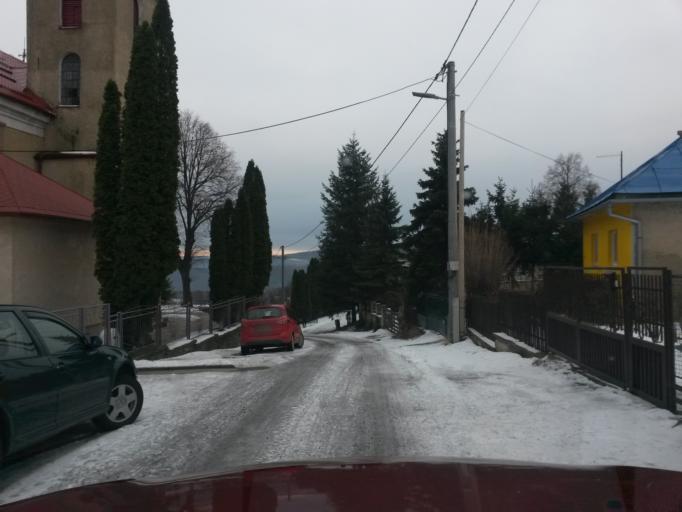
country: SK
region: Kosicky
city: Kosice
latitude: 48.7458
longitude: 21.1234
